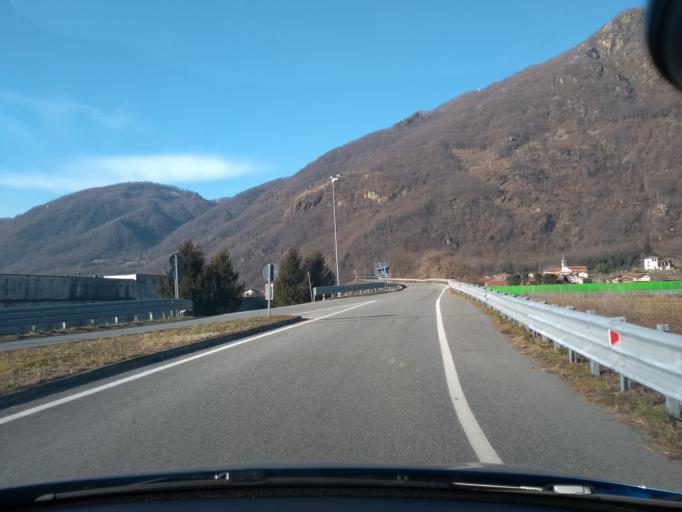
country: IT
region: Piedmont
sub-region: Provincia di Torino
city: Quassolo
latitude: 45.5082
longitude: 7.8351
